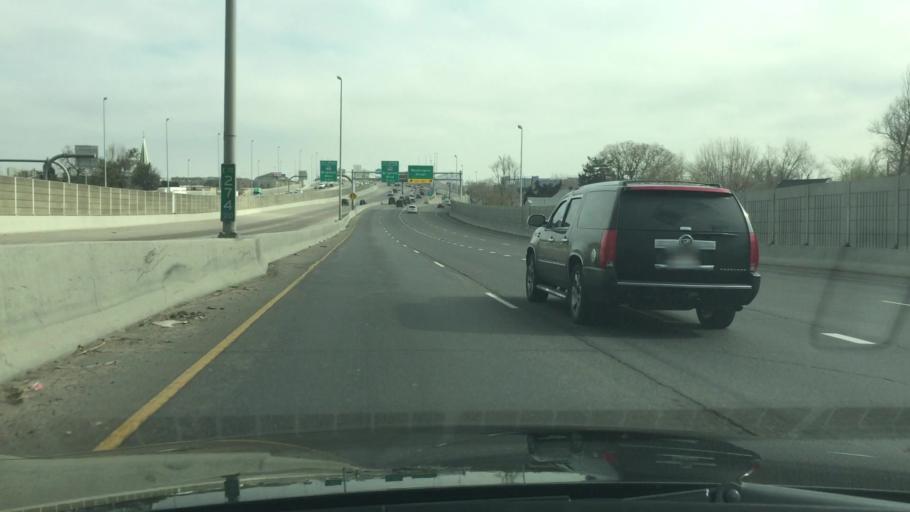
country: US
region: Colorado
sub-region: Denver County
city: Denver
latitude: 39.7796
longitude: -104.9846
